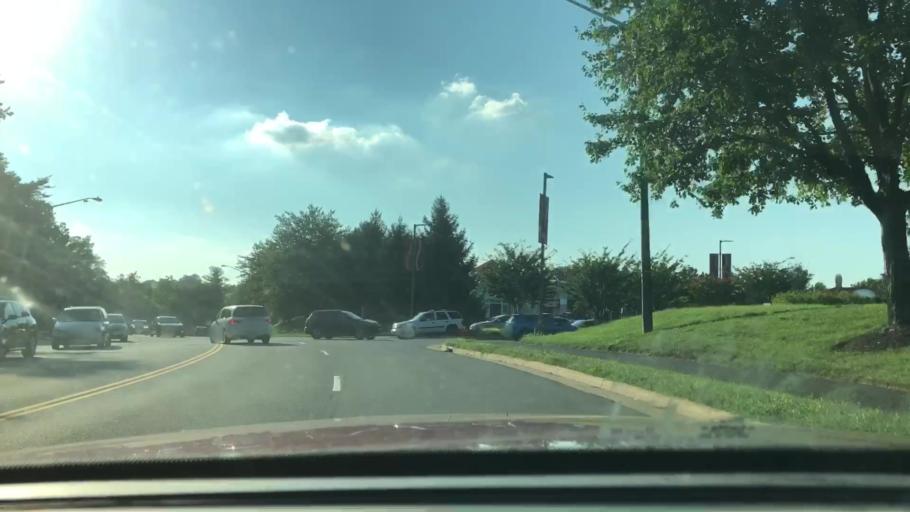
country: US
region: Virginia
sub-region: Fairfax County
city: Centreville
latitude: 38.8326
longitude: -77.4129
